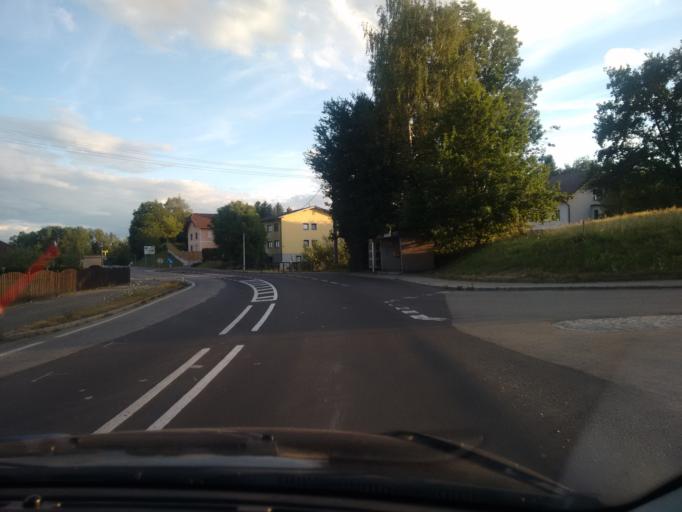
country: AT
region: Upper Austria
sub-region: Politischer Bezirk Grieskirchen
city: Bad Schallerbach
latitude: 48.2254
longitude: 13.9641
